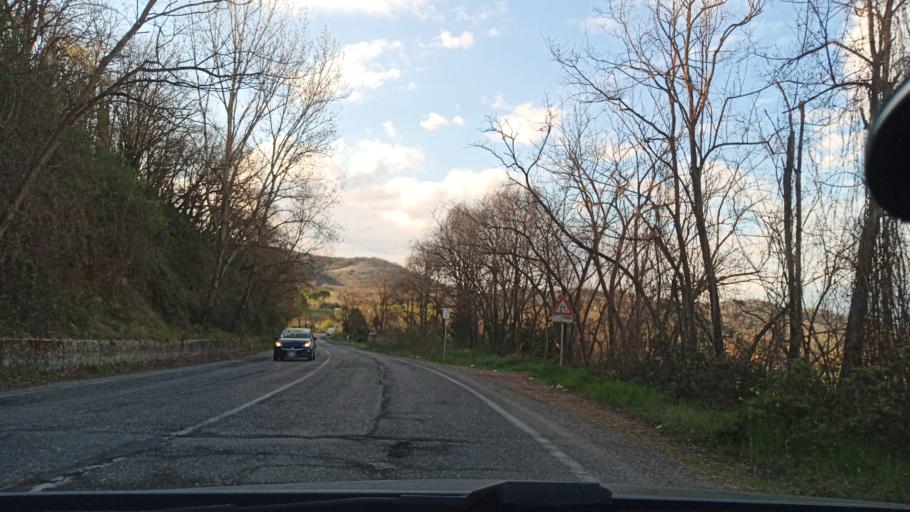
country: IT
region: Latium
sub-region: Citta metropolitana di Roma Capitale
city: Fiano Romano
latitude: 42.1792
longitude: 12.6074
